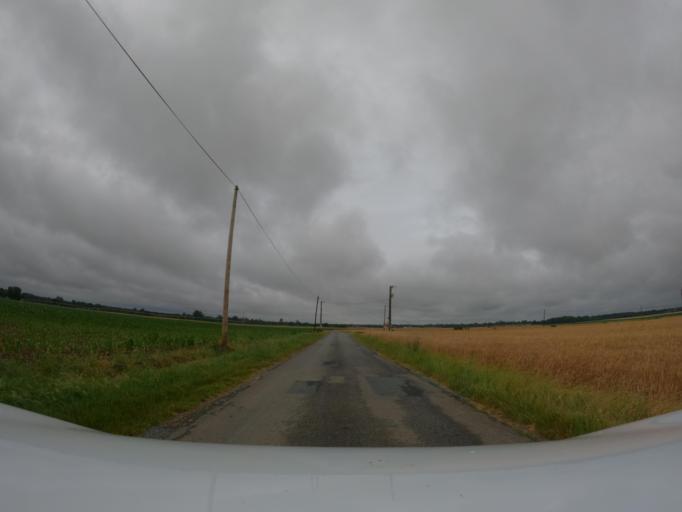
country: FR
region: Pays de la Loire
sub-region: Departement de la Vendee
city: Maillezais
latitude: 46.4020
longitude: -0.7165
